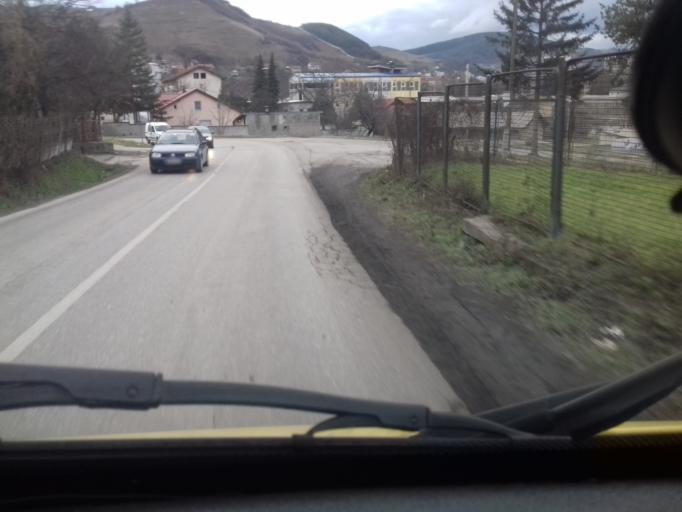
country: BA
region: Federation of Bosnia and Herzegovina
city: Zenica
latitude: 44.1883
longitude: 17.9279
